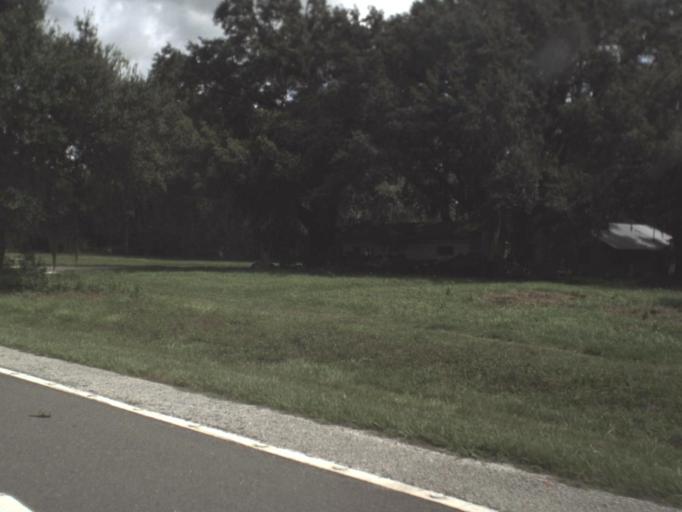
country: US
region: Florida
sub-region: Hardee County
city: Zolfo Springs
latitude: 27.3522
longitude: -81.8018
